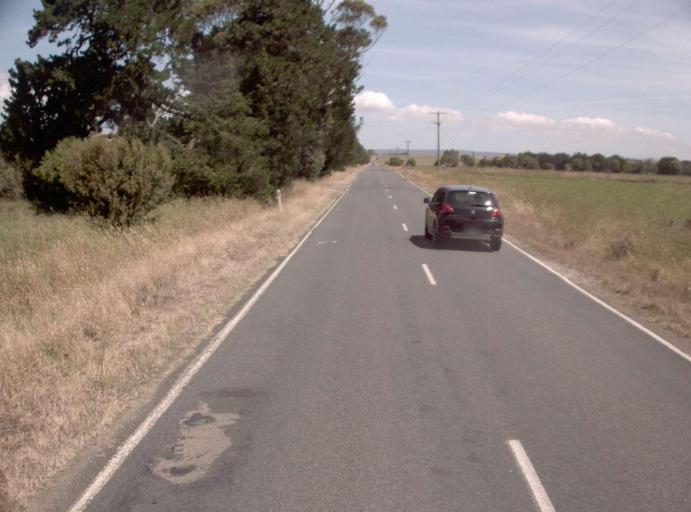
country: AU
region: Victoria
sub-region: Wellington
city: Heyfield
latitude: -38.0937
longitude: 146.8658
